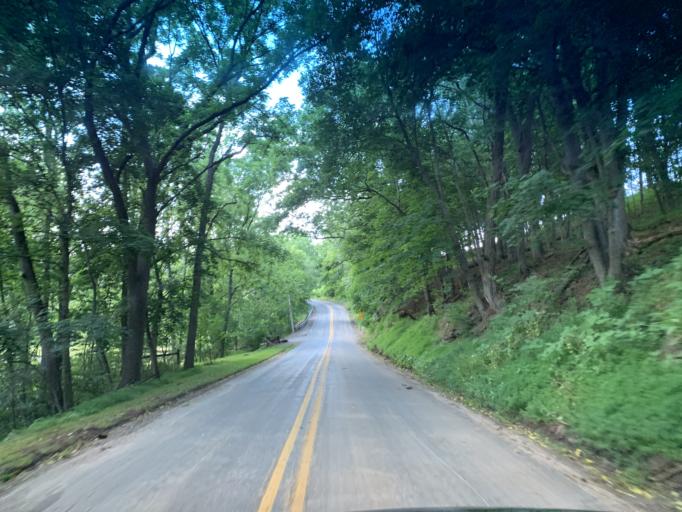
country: US
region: Pennsylvania
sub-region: York County
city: Stewartstown
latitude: 39.7495
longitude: -76.5400
